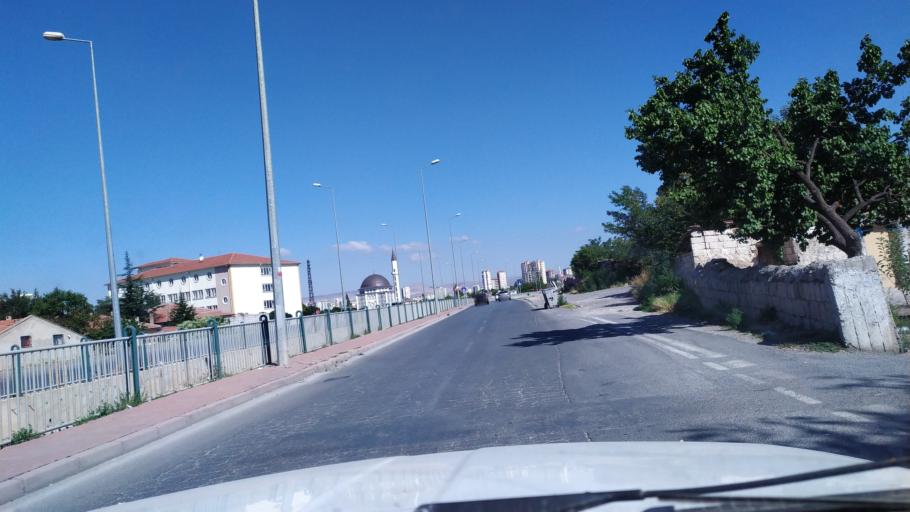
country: TR
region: Kayseri
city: Talas
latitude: 38.7285
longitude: 35.5503
